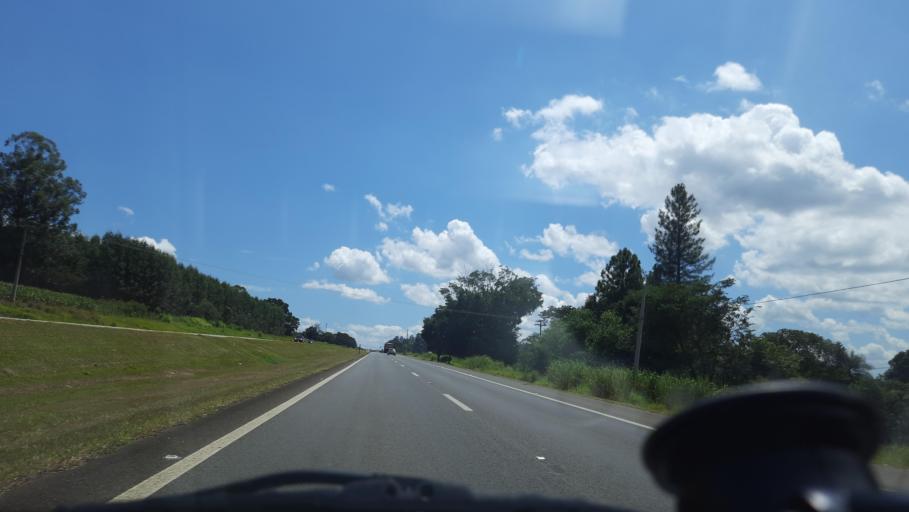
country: BR
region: Sao Paulo
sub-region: Moji-Guacu
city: Mogi-Gaucu
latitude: -22.2389
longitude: -46.9782
